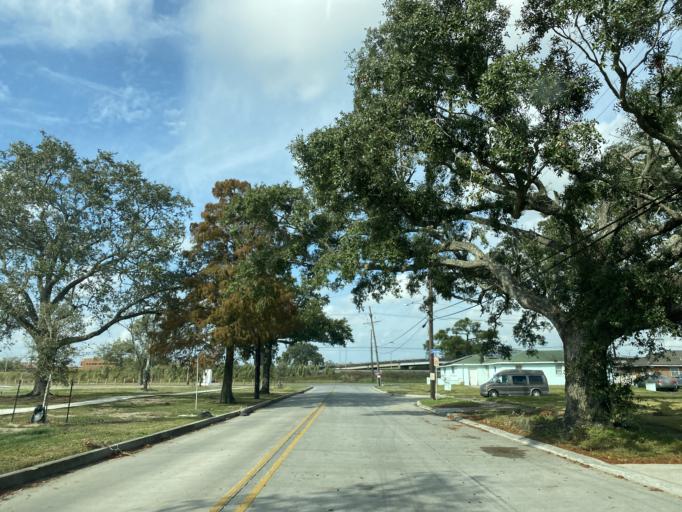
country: US
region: Louisiana
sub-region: Saint Bernard Parish
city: Arabi
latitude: 30.0291
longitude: -90.0386
